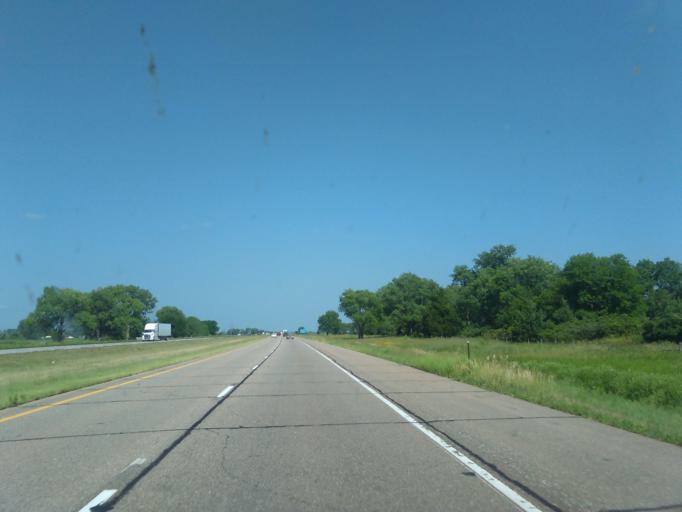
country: US
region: Nebraska
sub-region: Buffalo County
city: Kearney
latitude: 40.6700
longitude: -99.1450
